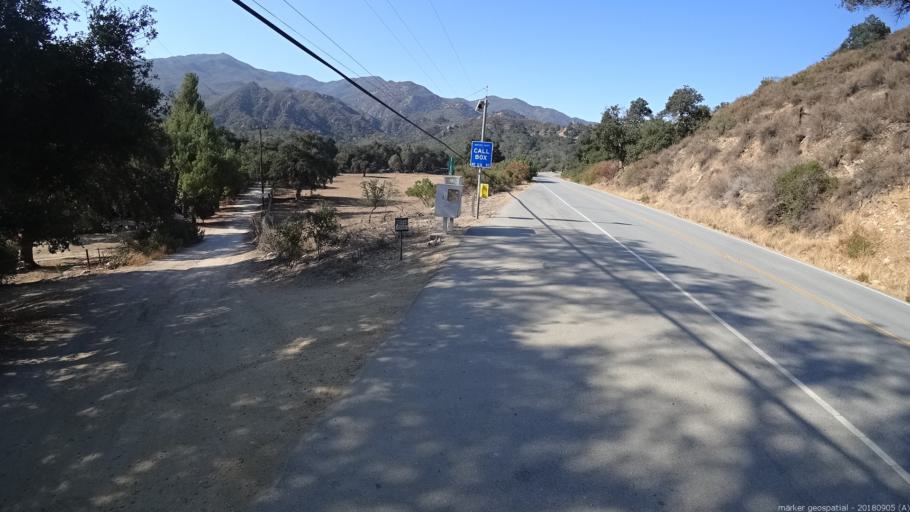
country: US
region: California
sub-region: Monterey County
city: Greenfield
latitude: 36.2419
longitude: -121.4330
